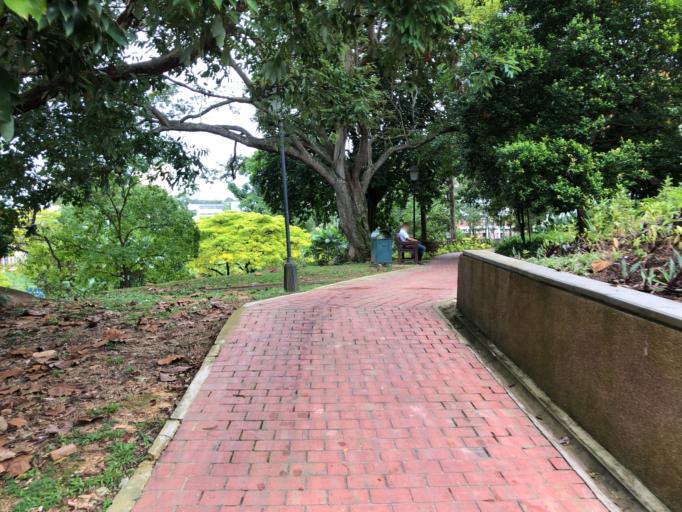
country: SG
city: Singapore
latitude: 1.2966
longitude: 103.8457
